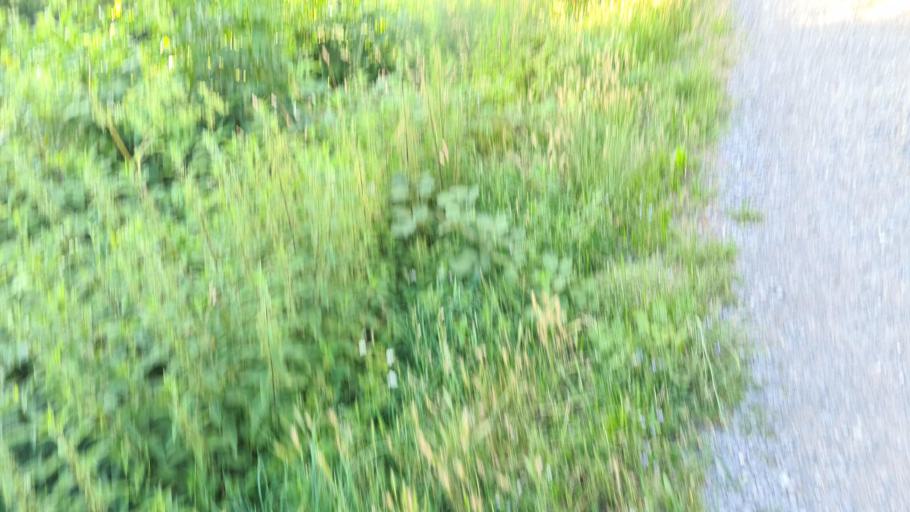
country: DE
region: Hesse
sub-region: Regierungsbezirk Darmstadt
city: Nauheim
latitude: 49.9631
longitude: 8.4461
